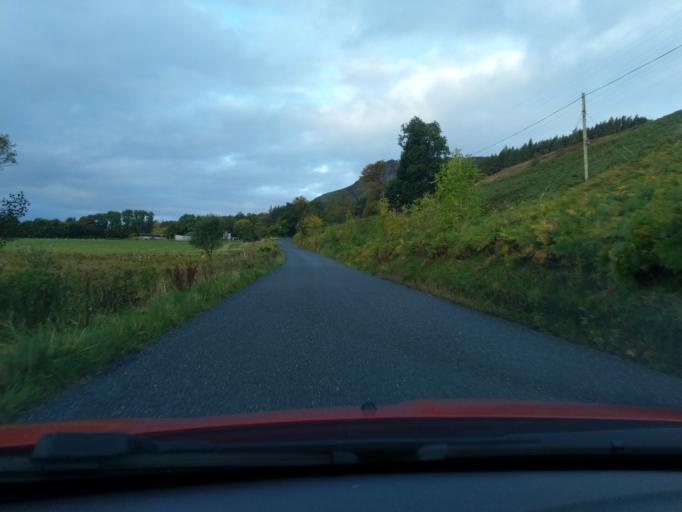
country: GB
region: Scotland
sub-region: Perth and Kinross
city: Aberfeldy
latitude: 56.7014
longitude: -4.1464
